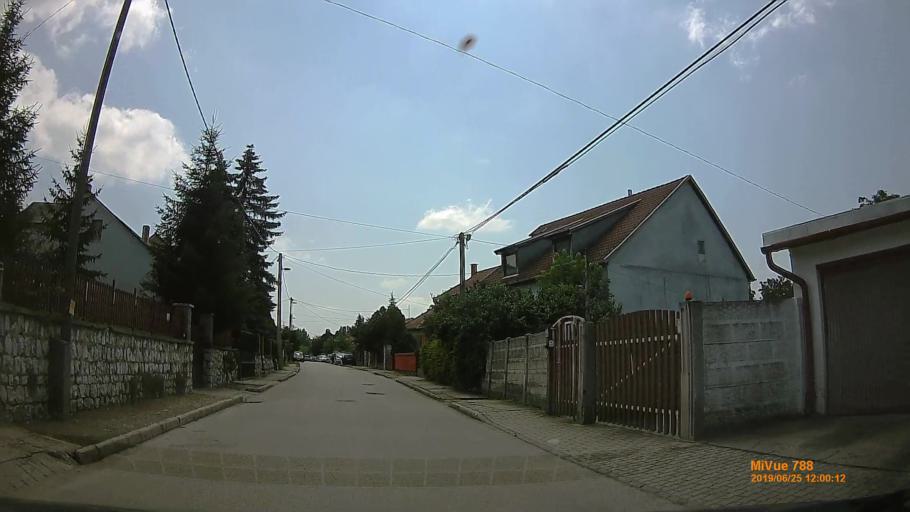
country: HU
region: Komarom-Esztergom
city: Dorog
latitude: 47.7285
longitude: 18.7348
